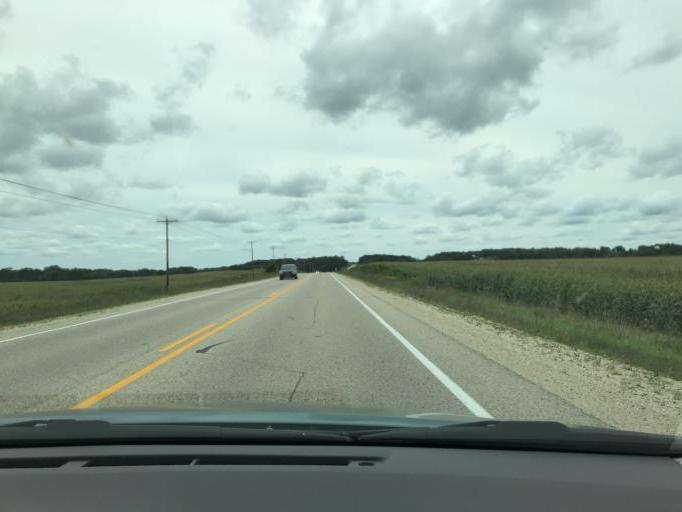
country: US
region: Wisconsin
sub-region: Racine County
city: Bohners Lake
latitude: 42.6158
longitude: -88.2338
